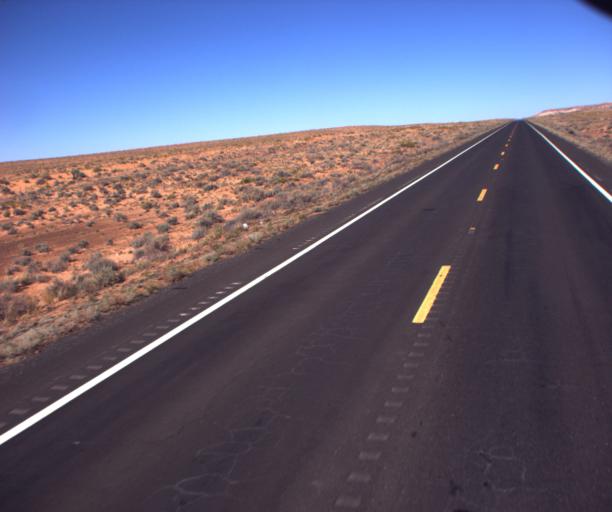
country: US
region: Arizona
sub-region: Coconino County
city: Tuba City
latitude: 36.2023
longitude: -111.0571
